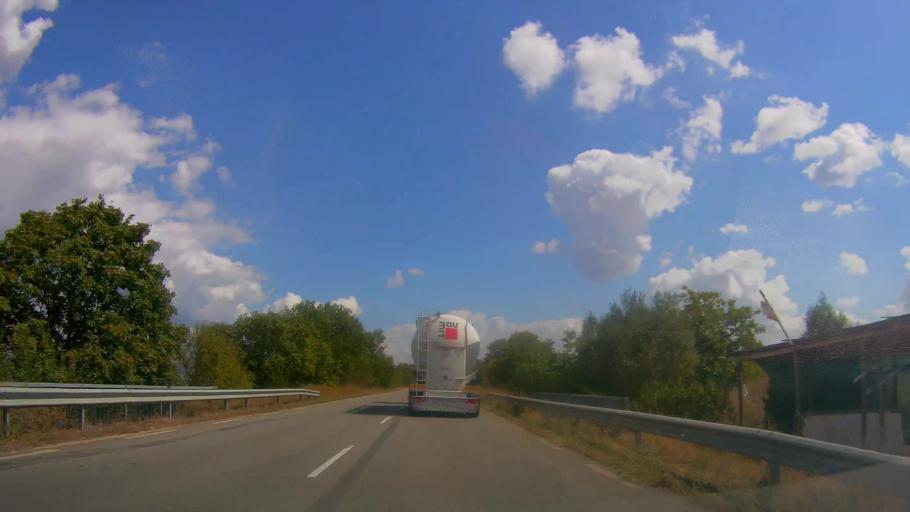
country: BG
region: Sliven
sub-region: Obshtina Tvurditsa
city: Tvurditsa
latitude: 42.6568
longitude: 25.9260
